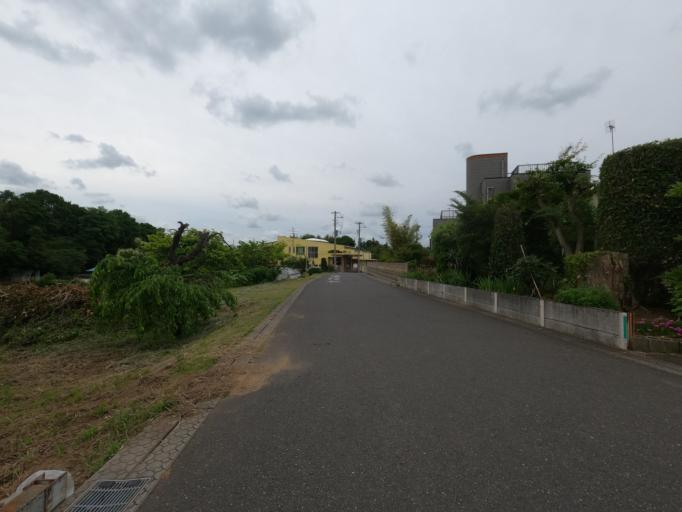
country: JP
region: Ibaraki
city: Moriya
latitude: 35.9491
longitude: 139.9713
